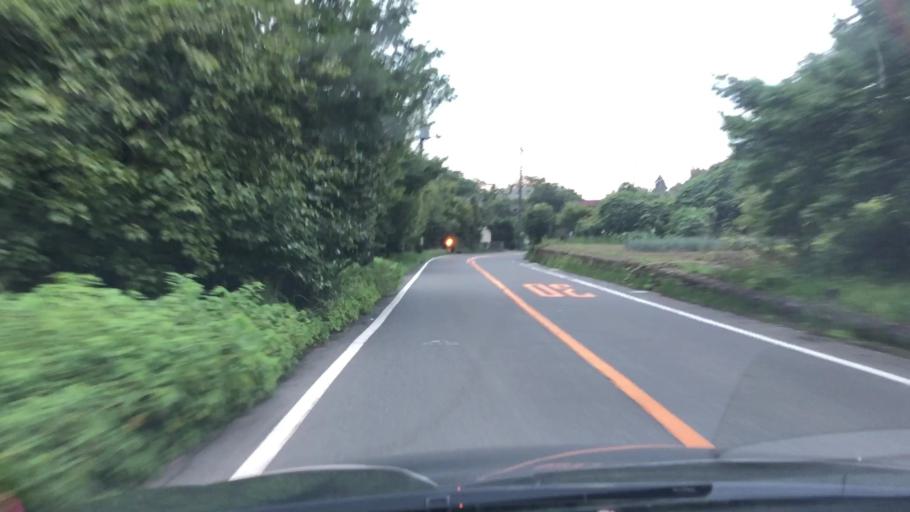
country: JP
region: Tokyo
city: Ome
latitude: 35.7577
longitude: 139.2348
